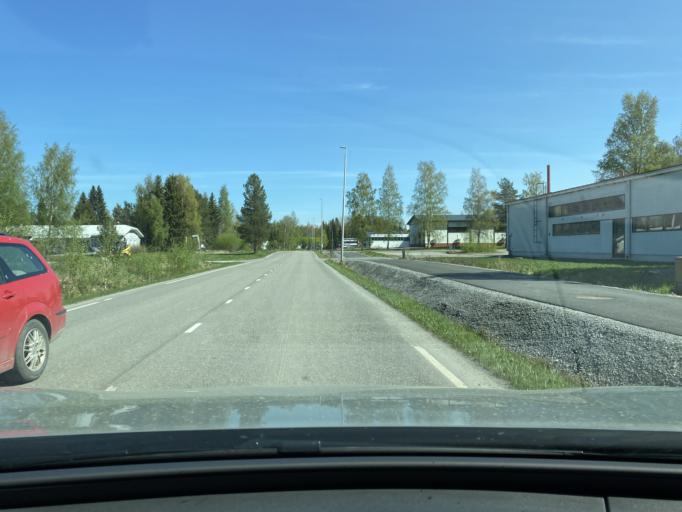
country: FI
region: Pirkanmaa
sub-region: Lounais-Pirkanmaa
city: Vammala
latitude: 61.3296
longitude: 22.9118
